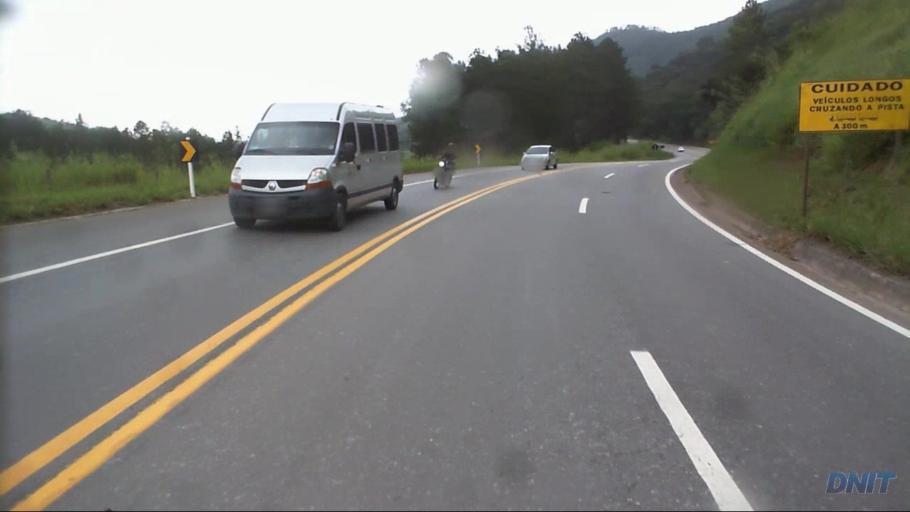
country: BR
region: Minas Gerais
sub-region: Nova Era
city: Nova Era
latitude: -19.7258
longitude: -43.0097
